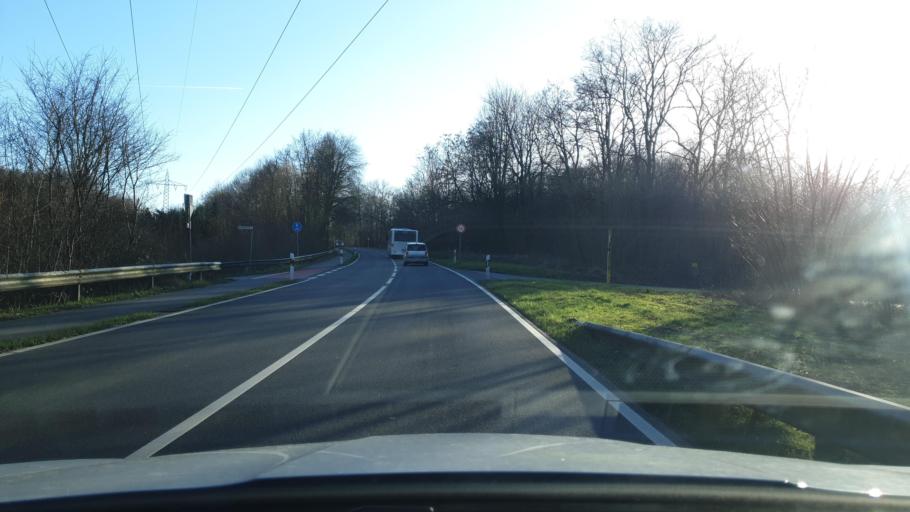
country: DE
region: North Rhine-Westphalia
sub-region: Regierungsbezirk Detmold
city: Hiddenhausen
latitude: 52.1800
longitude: 8.6180
